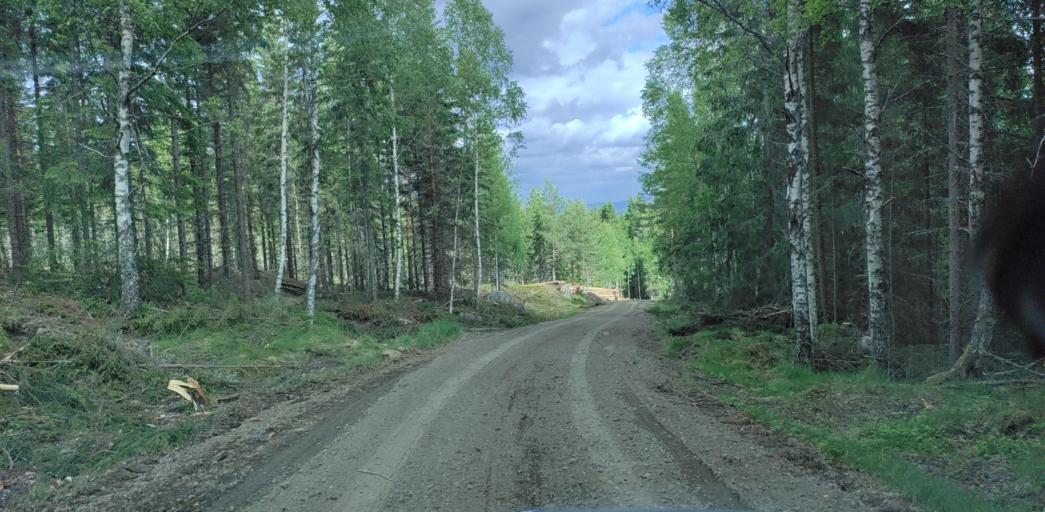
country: SE
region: Vaermland
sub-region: Munkfors Kommun
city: Munkfors
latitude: 59.9703
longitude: 13.3987
